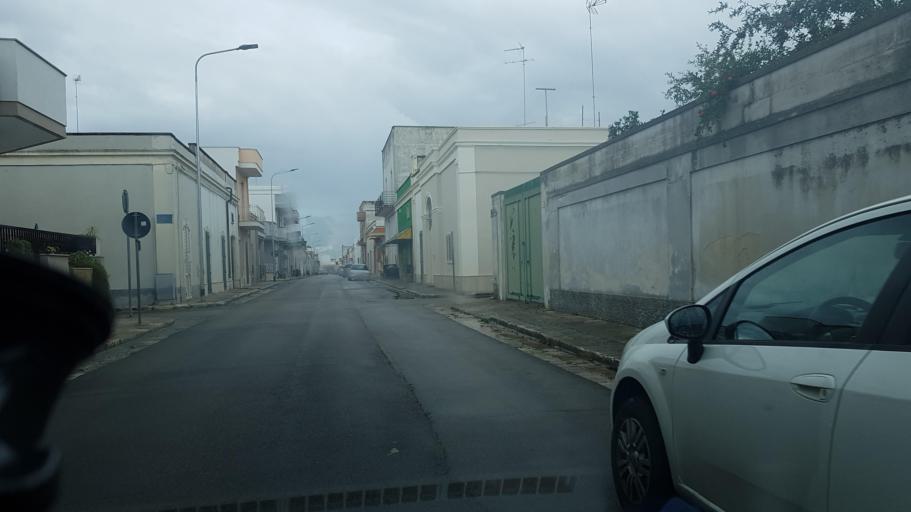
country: IT
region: Apulia
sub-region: Provincia di Lecce
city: Carmiano
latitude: 40.3452
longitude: 18.0423
